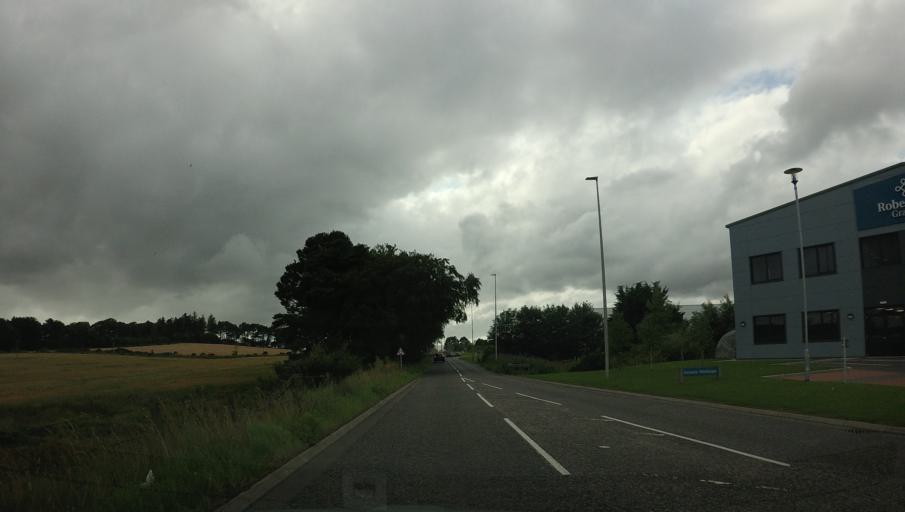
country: GB
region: Scotland
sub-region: Aberdeenshire
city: Westhill
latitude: 57.1442
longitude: -2.2873
